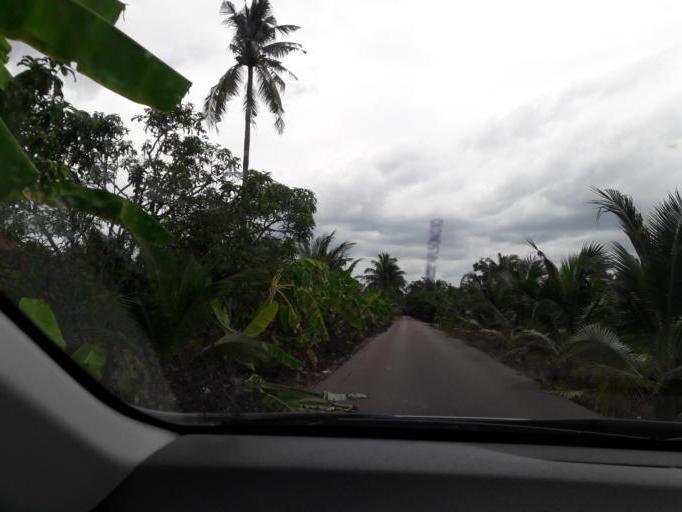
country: TH
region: Ratchaburi
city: Damnoen Saduak
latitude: 13.5464
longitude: 99.9983
